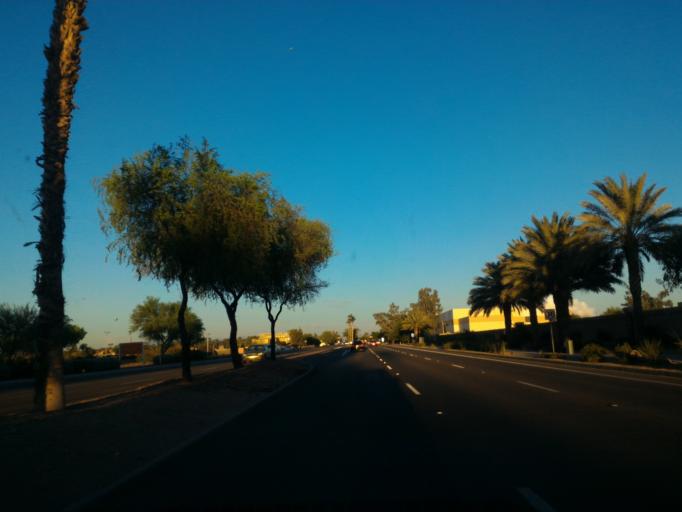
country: US
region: Arizona
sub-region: Maricopa County
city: Chandler
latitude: 33.3054
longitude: -111.9169
